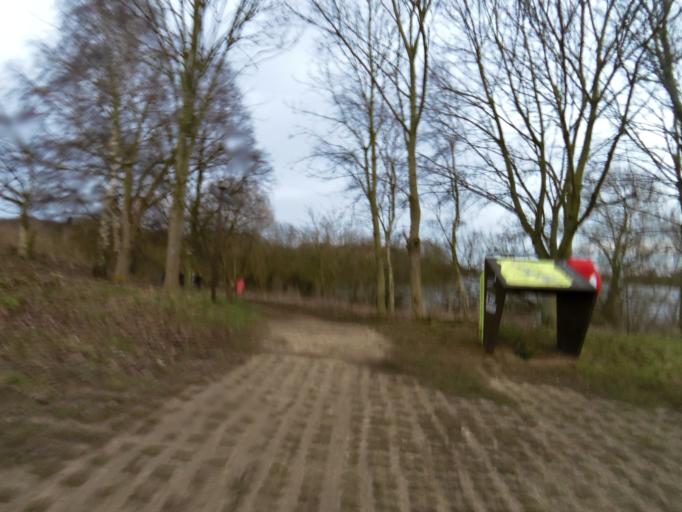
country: GB
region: England
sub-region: Essex
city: Mistley
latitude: 51.9964
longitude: 1.1120
